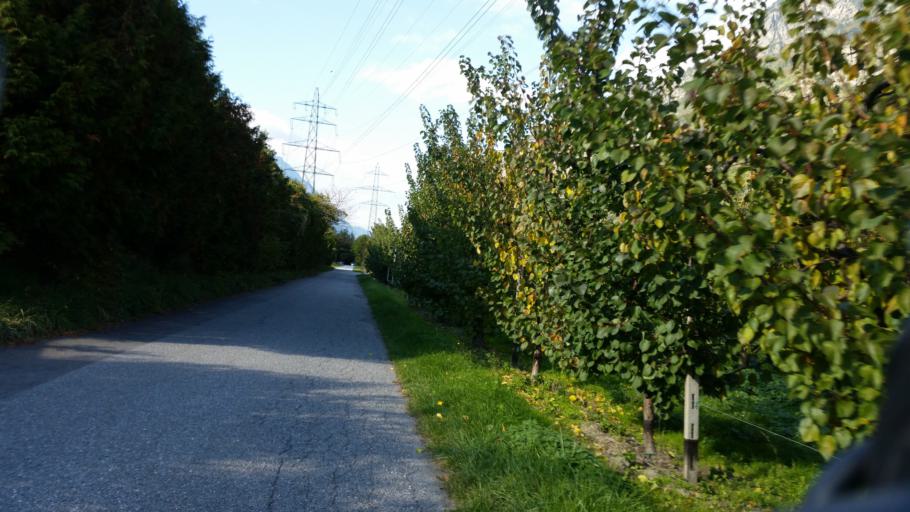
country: CH
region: Valais
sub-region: Martigny District
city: Martigny-Ville
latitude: 46.1225
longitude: 7.0640
